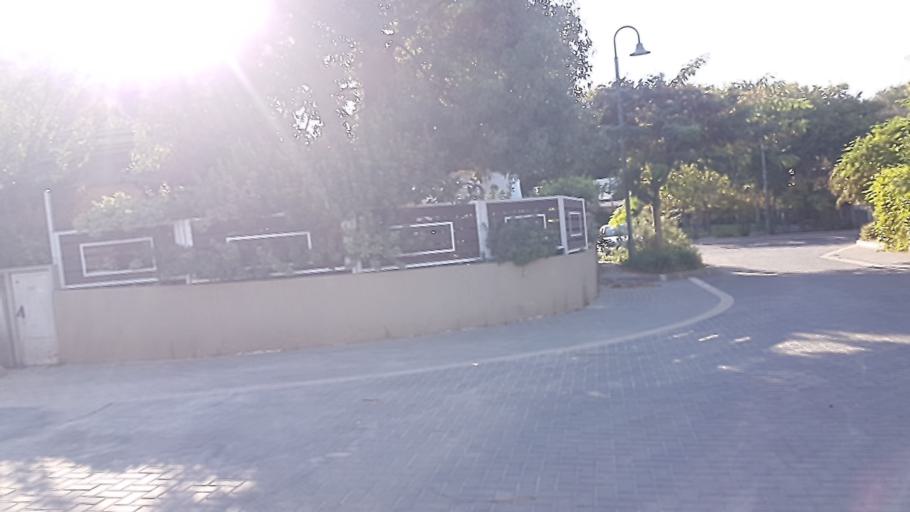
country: IL
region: Central District
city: Hod HaSharon
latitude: 32.1384
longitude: 34.9090
